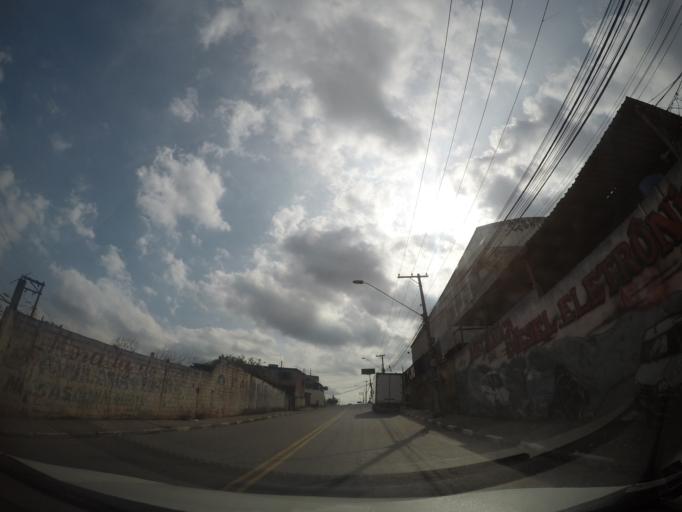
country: BR
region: Sao Paulo
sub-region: Guarulhos
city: Guarulhos
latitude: -23.4157
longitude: -46.4536
